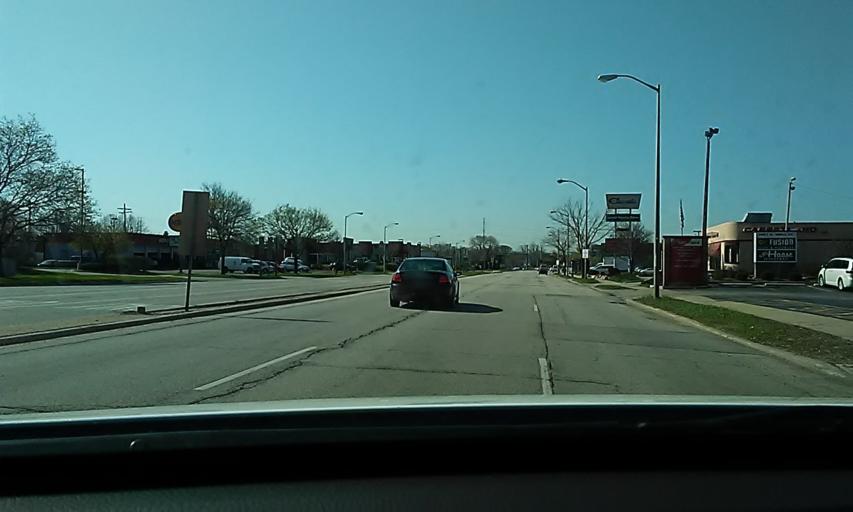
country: US
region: Wisconsin
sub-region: Milwaukee County
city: West Allis
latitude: 43.0162
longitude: -88.0471
